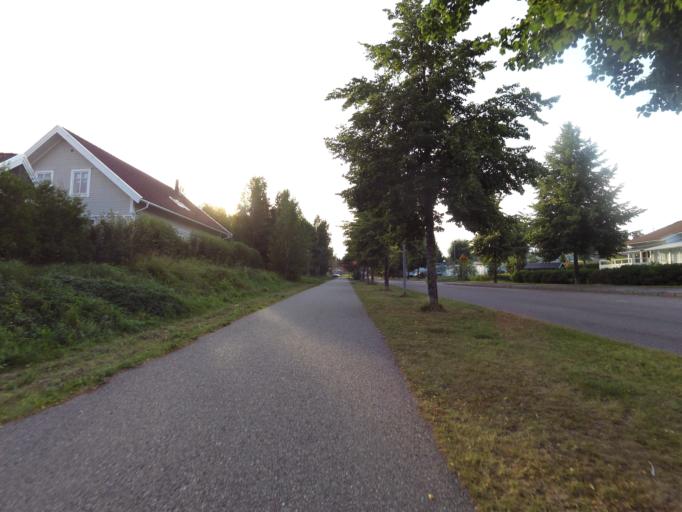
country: SE
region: Gaevleborg
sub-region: Gavle Kommun
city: Gavle
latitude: 60.7011
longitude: 17.1010
